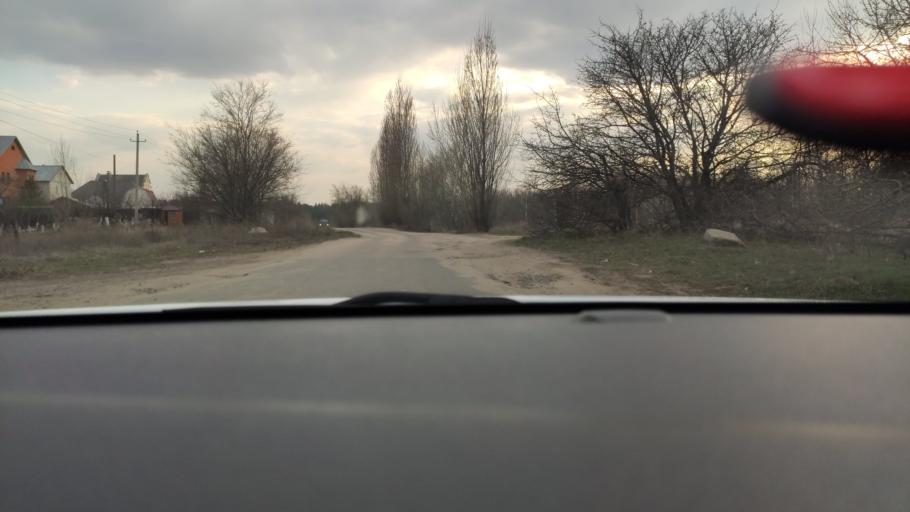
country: RU
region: Voronezj
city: Pridonskoy
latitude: 51.6386
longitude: 39.0915
